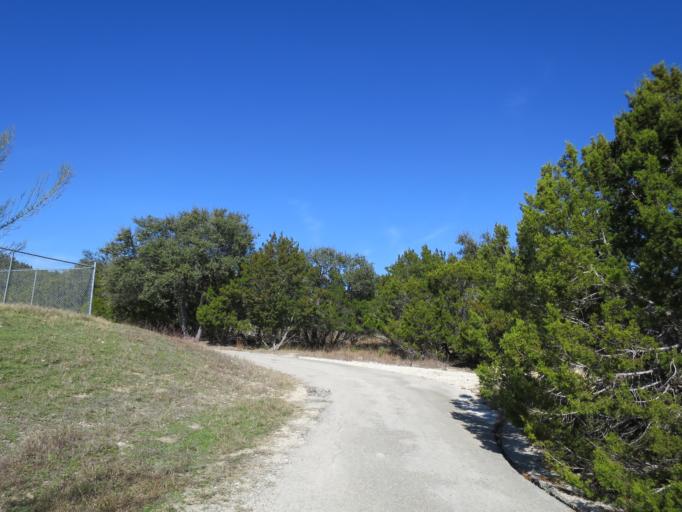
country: US
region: Texas
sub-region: Travis County
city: Lakeway
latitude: 30.3808
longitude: -97.9670
